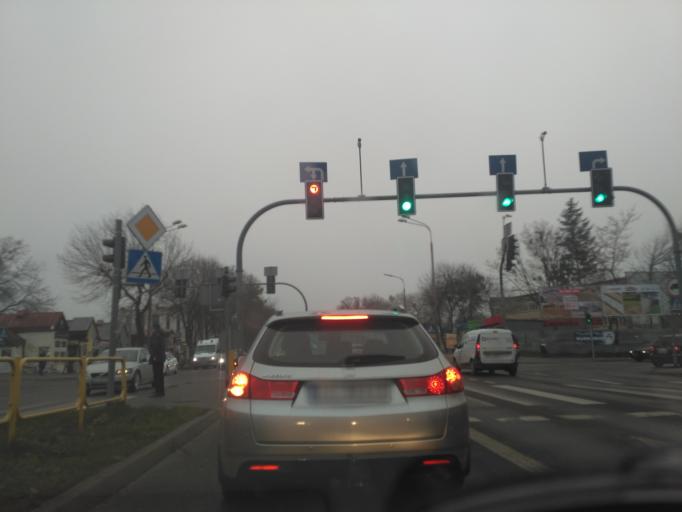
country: PL
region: Lublin Voivodeship
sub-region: Chelm
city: Chelm
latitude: 51.1295
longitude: 23.4701
